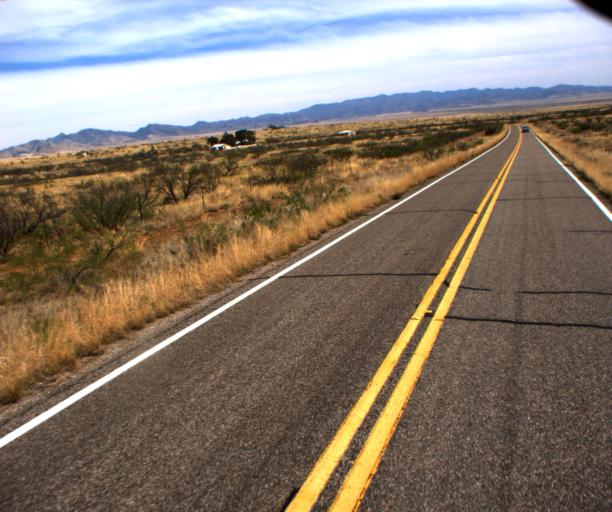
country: US
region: Arizona
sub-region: Cochise County
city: Willcox
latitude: 32.1352
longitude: -109.5611
